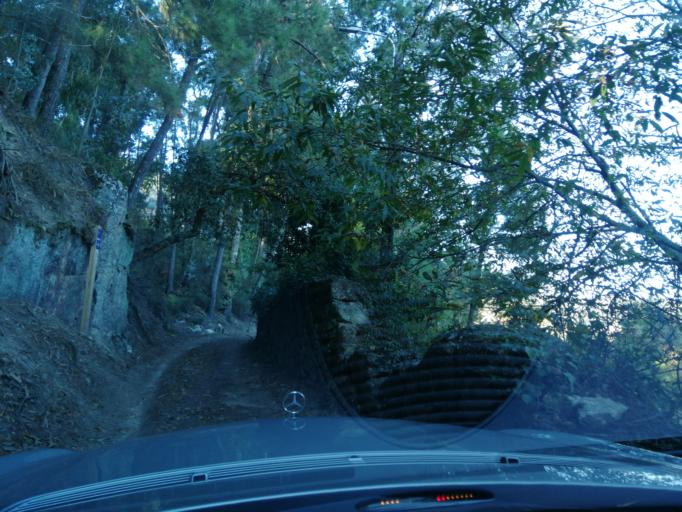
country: PT
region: Braga
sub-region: Braga
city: Oliveira
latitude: 41.4550
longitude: -8.4598
